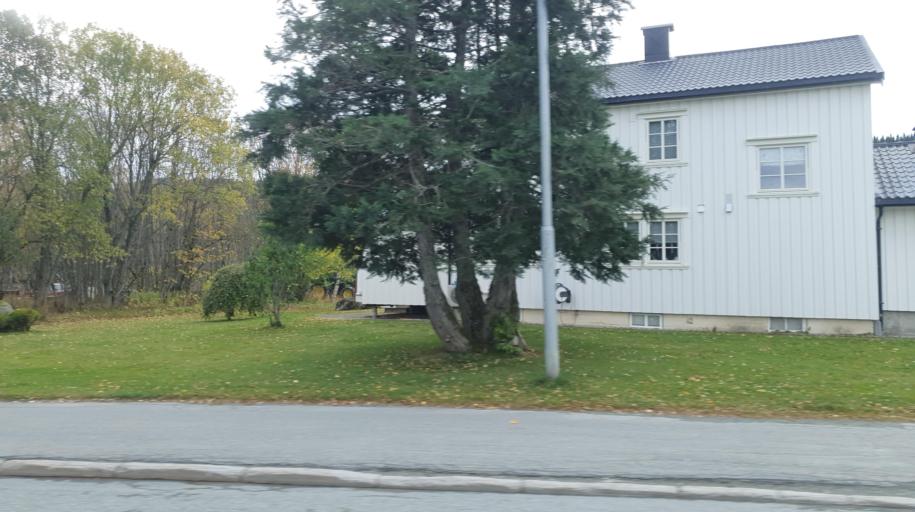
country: NO
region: Sor-Trondelag
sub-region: Klaebu
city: Klaebu
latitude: 63.3083
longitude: 10.4310
